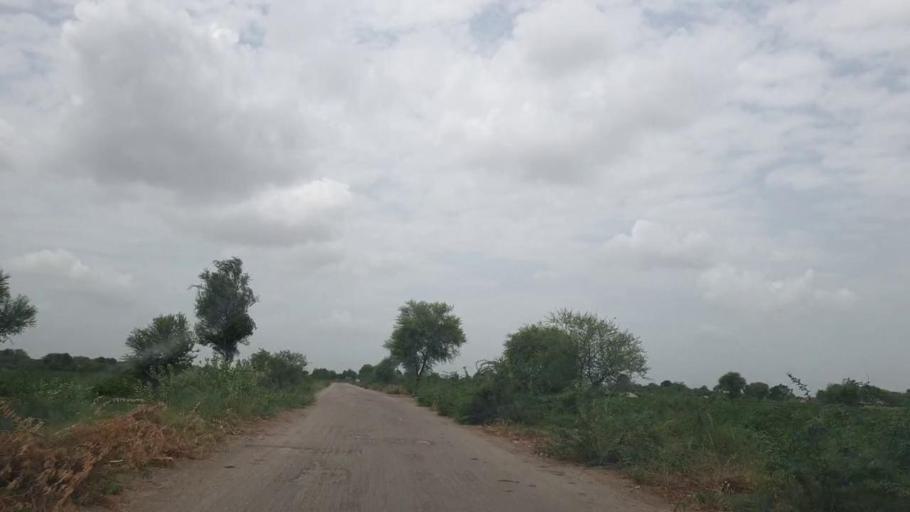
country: PK
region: Sindh
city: Naukot
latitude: 24.9095
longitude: 69.2663
